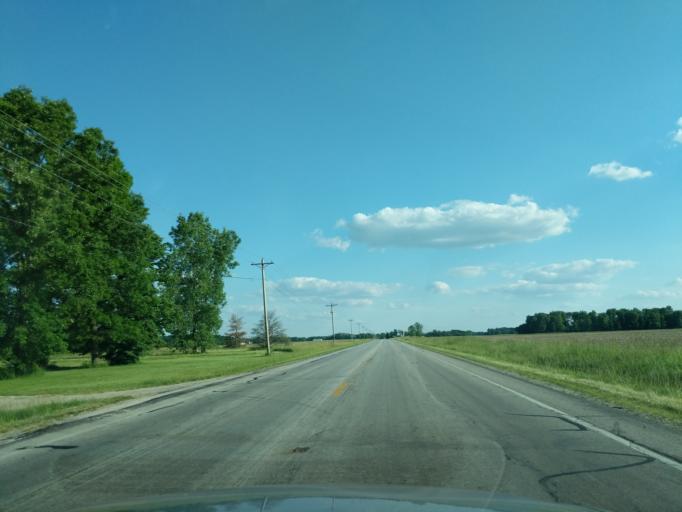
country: US
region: Indiana
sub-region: Whitley County
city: Tri-Lakes
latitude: 41.3025
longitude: -85.5002
